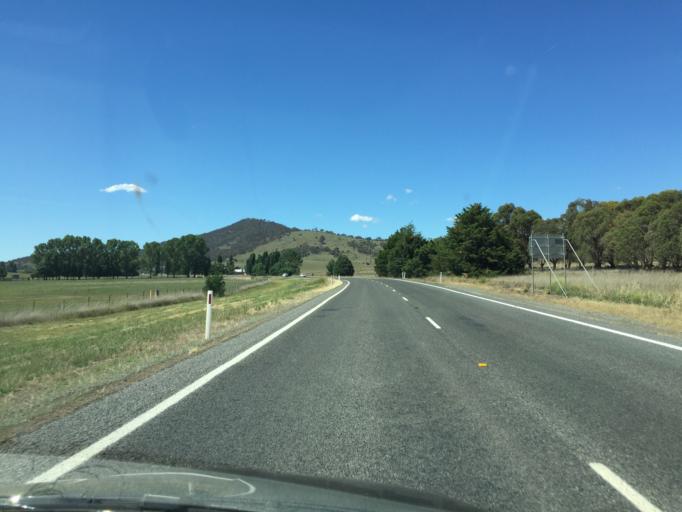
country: AU
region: Australian Capital Territory
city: Macarthur
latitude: -35.6997
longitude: 149.1607
